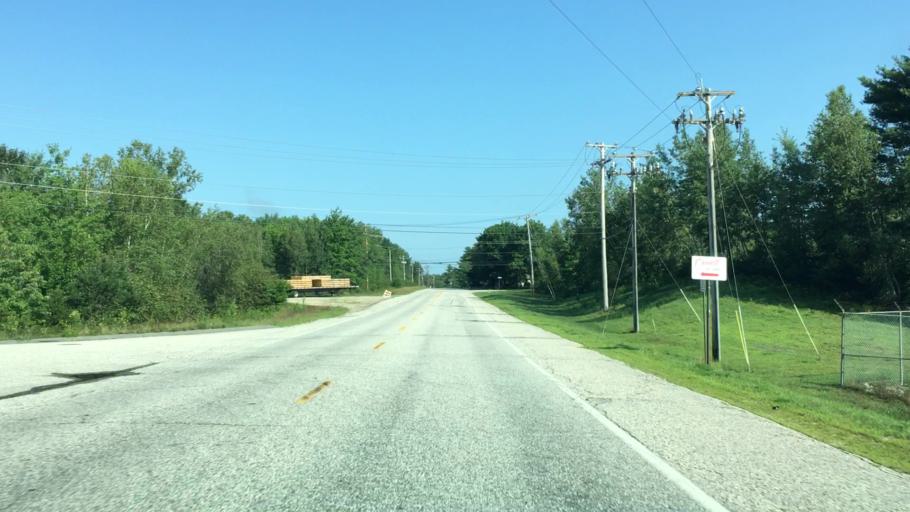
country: US
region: Maine
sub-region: Androscoggin County
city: Minot
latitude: 44.0417
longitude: -70.2914
